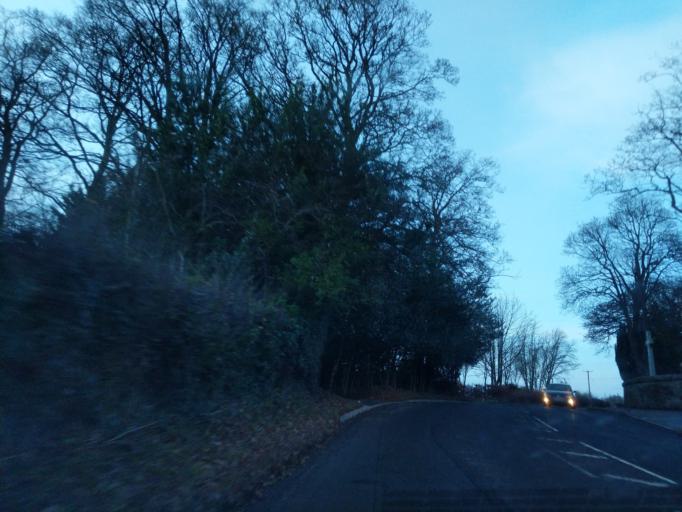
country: GB
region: Scotland
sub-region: Midlothian
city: Bonnyrigg
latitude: 55.8658
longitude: -3.0897
